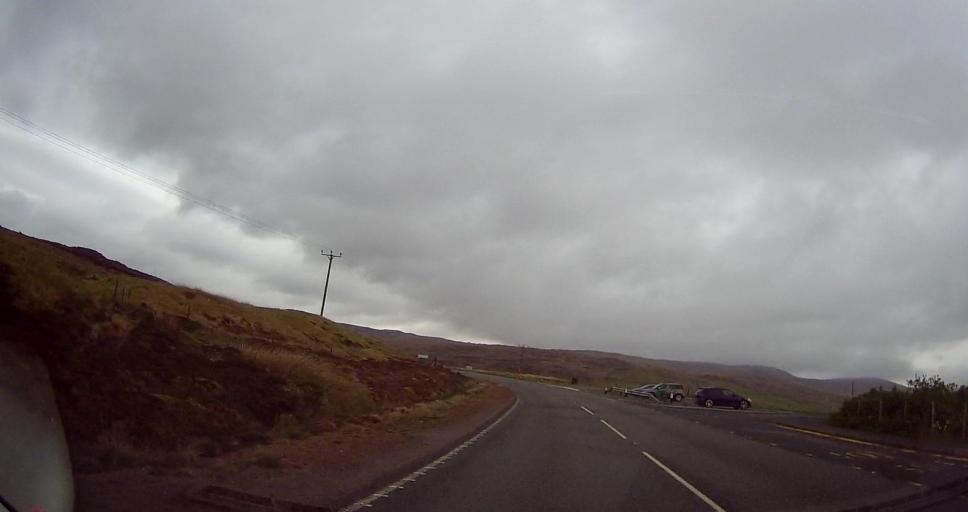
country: GB
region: Scotland
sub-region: Shetland Islands
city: Lerwick
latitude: 60.2635
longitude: -1.2221
